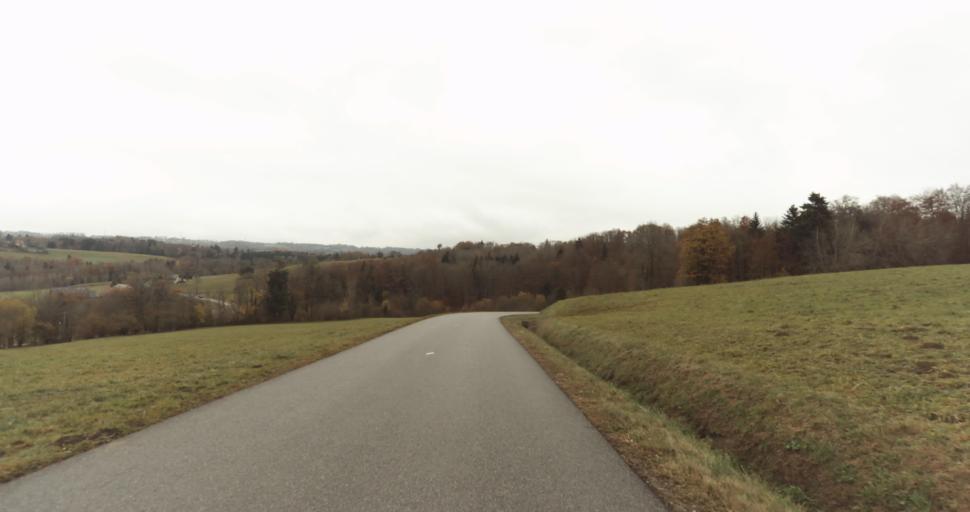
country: FR
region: Rhone-Alpes
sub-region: Departement de la Haute-Savoie
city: Evires
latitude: 46.0314
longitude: 6.2440
